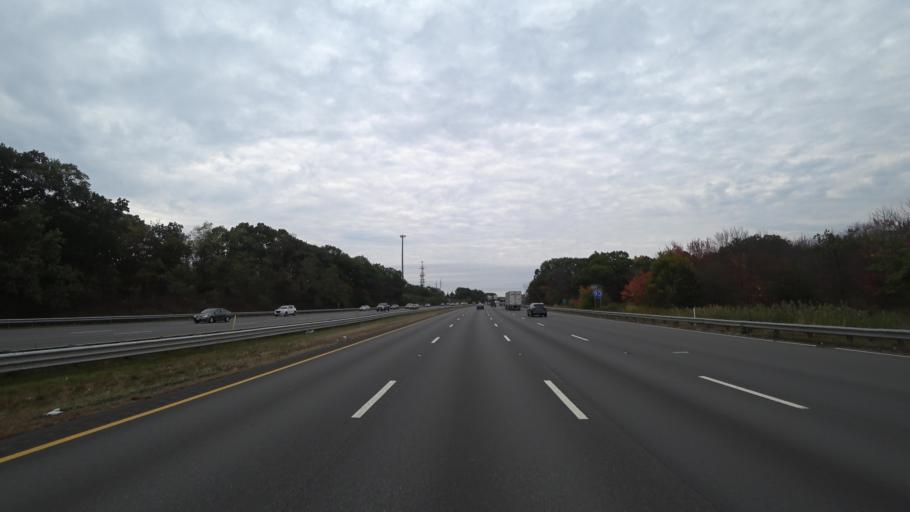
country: US
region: Massachusetts
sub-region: Middlesex County
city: Reading
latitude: 42.5261
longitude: -71.1357
